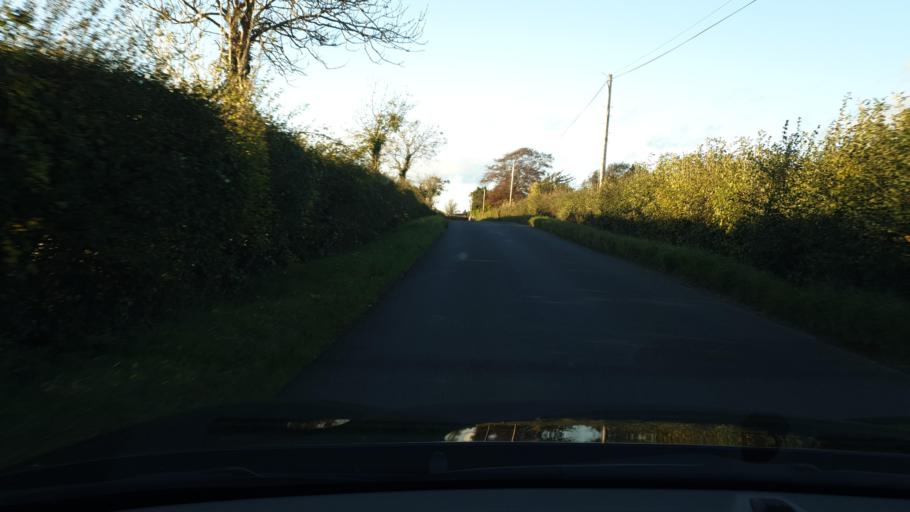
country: IE
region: Leinster
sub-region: Lu
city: Drogheda
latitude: 53.6865
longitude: -6.3352
